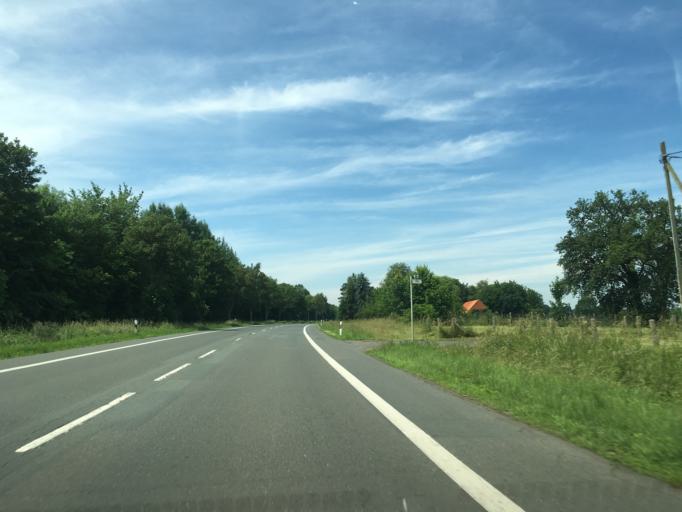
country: DE
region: North Rhine-Westphalia
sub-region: Regierungsbezirk Munster
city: Steinfurt
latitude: 52.1468
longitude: 7.4032
